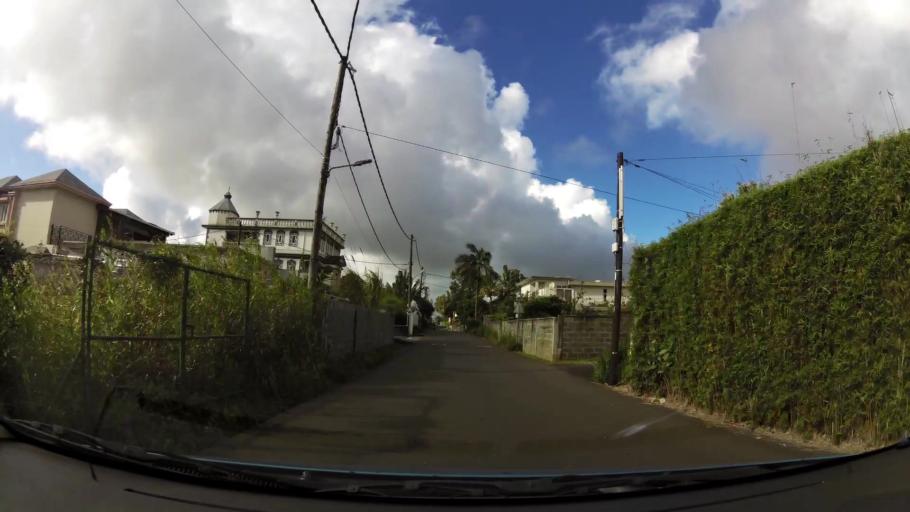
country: MU
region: Plaines Wilhems
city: Curepipe
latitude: -20.3280
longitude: 57.5192
